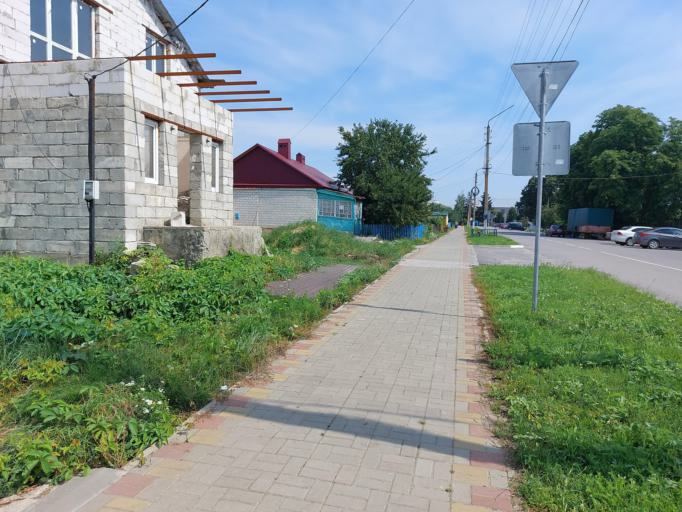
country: RU
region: Lipetsk
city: Dolgorukovo
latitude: 52.3245
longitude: 38.3600
